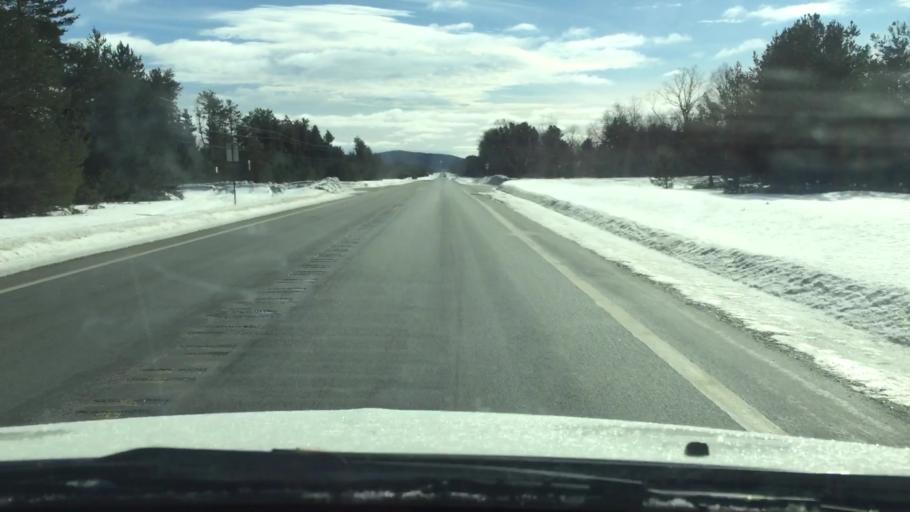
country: US
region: Michigan
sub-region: Antrim County
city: Mancelona
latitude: 44.9322
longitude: -85.0509
